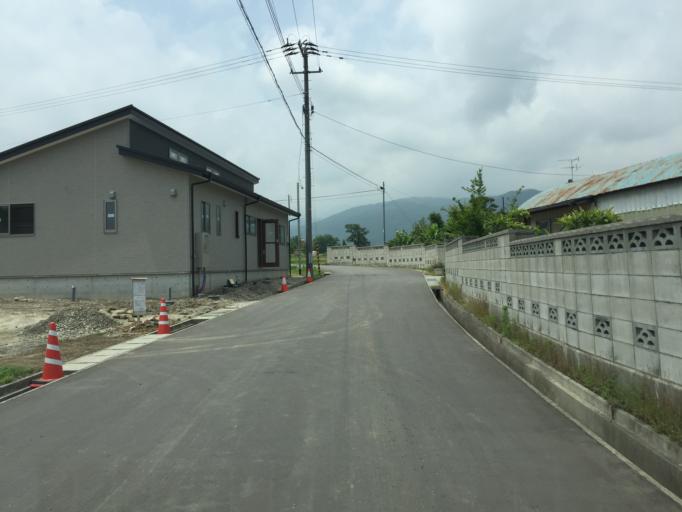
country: JP
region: Fukushima
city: Fukushima-shi
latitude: 37.7366
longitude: 140.3804
